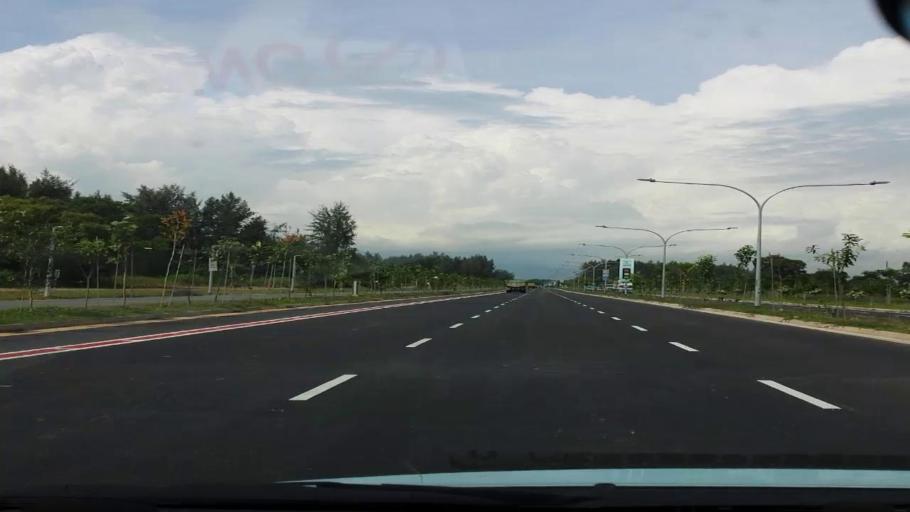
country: SG
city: Singapore
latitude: 1.3320
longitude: 104.0215
